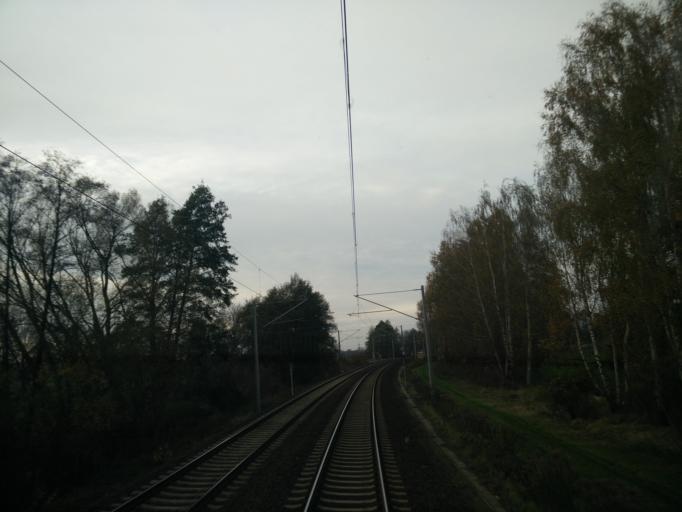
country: DE
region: Brandenburg
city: Lubbenau
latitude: 51.8742
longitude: 13.9238
